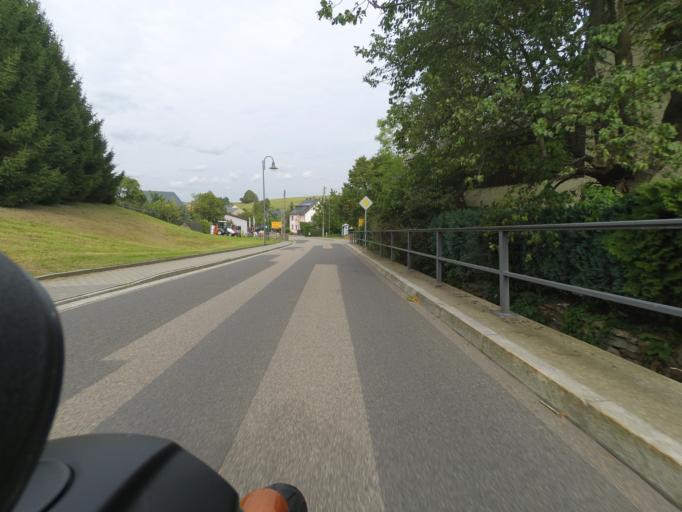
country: DE
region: Saxony
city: Barenstein
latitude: 50.8312
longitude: 13.8060
